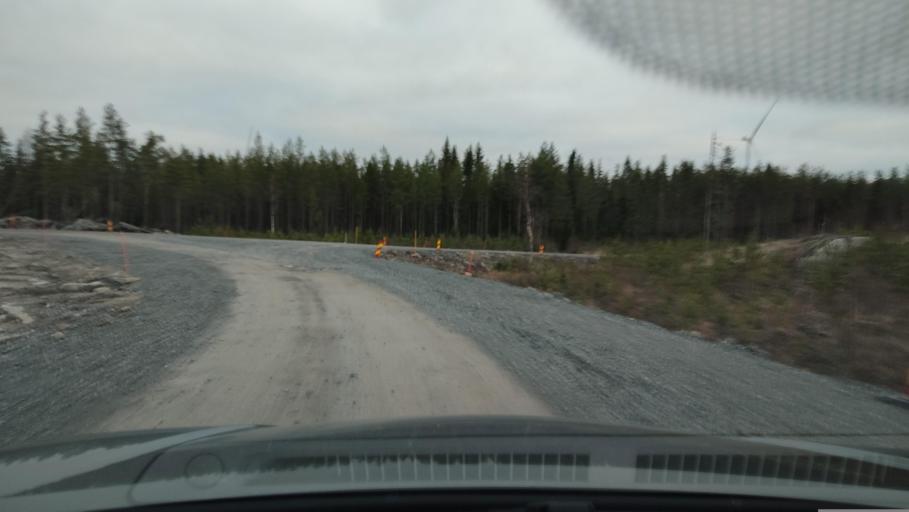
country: FI
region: Southern Ostrobothnia
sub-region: Suupohja
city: Karijoki
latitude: 62.1899
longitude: 21.5749
